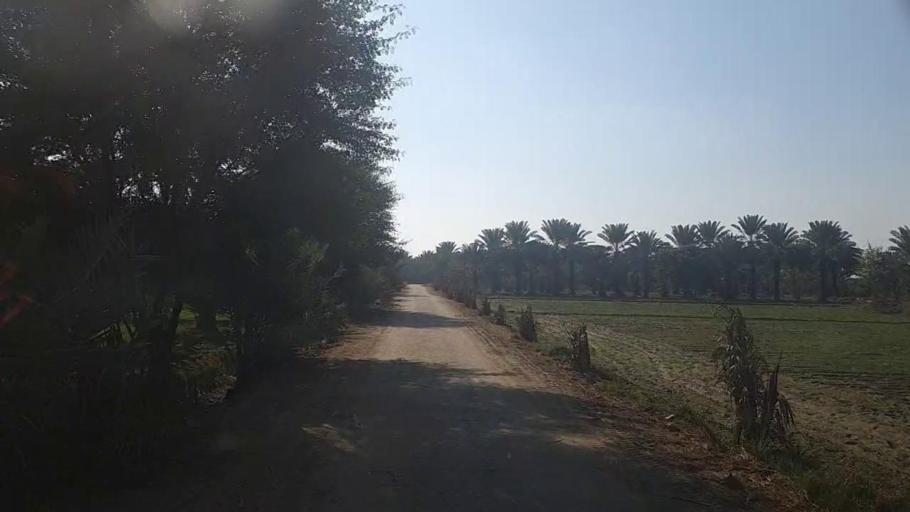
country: PK
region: Sindh
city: Khairpur
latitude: 27.4437
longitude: 68.7378
